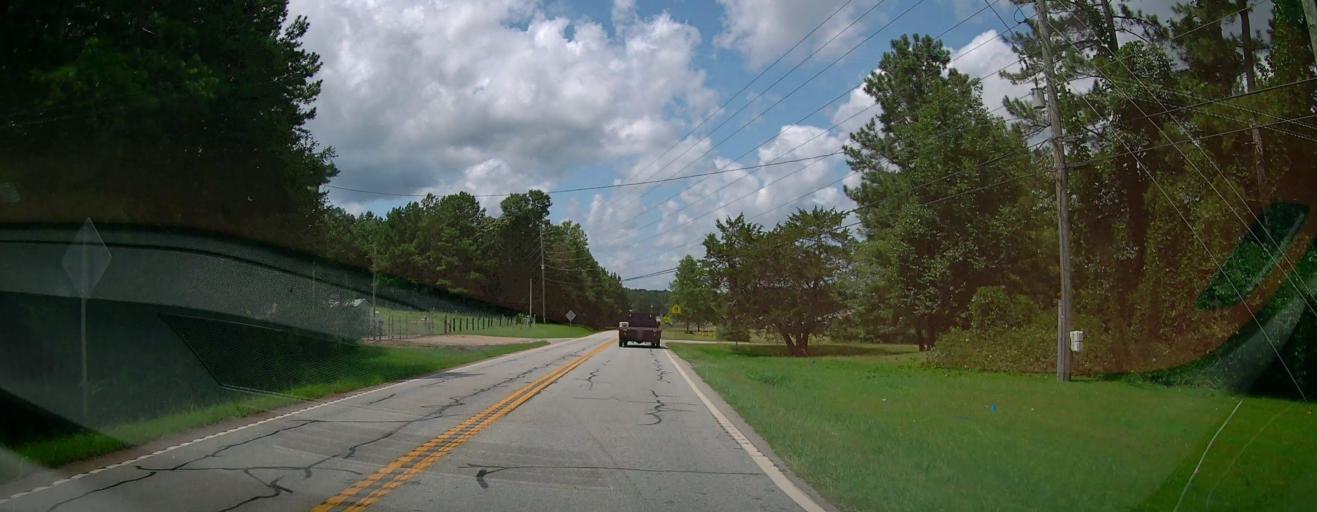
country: US
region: Georgia
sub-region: Heard County
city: Franklin
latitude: 33.2910
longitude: -85.1184
